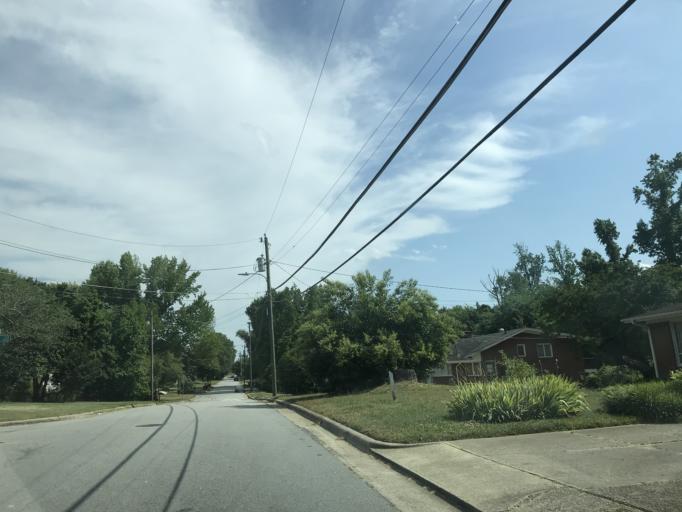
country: US
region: North Carolina
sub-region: Wake County
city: Raleigh
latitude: 35.7910
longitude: -78.6154
